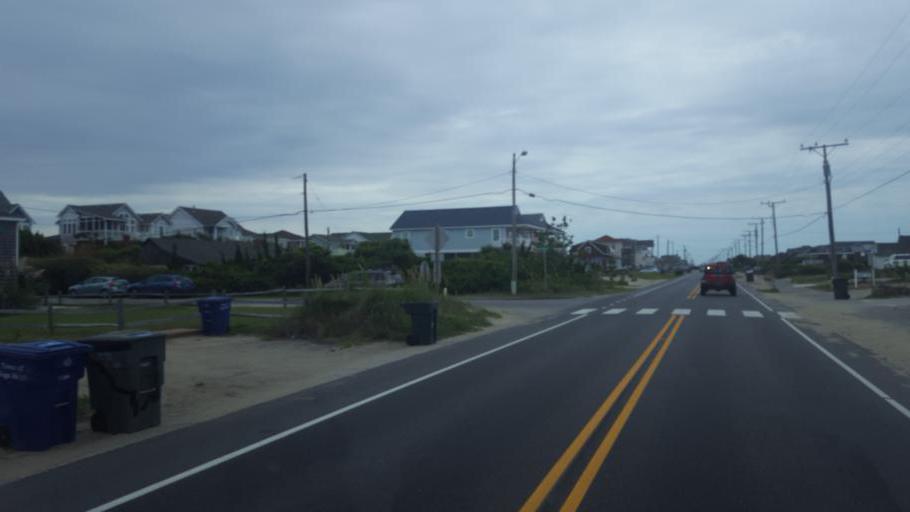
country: US
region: North Carolina
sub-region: Dare County
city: Nags Head
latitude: 35.9757
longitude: -75.6345
